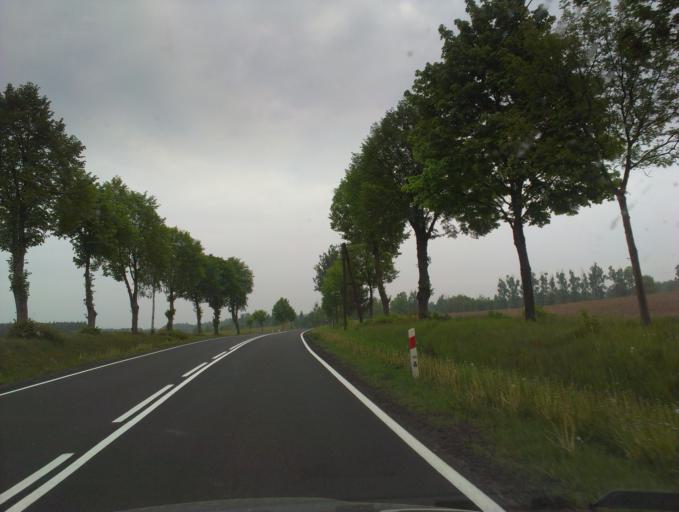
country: PL
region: West Pomeranian Voivodeship
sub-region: Powiat szczecinecki
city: Szczecinek
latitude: 53.8055
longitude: 16.6416
